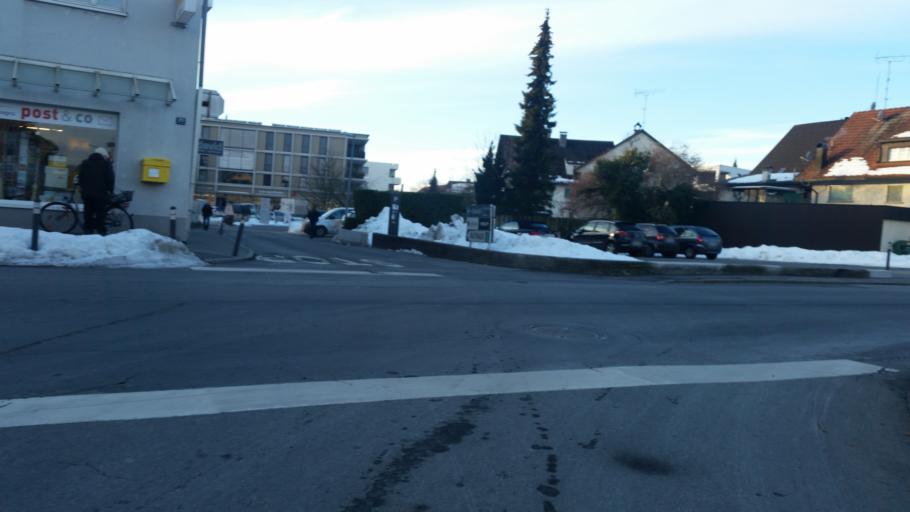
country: AT
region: Vorarlberg
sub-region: Politischer Bezirk Bregenz
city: Hard
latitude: 47.4902
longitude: 9.6933
